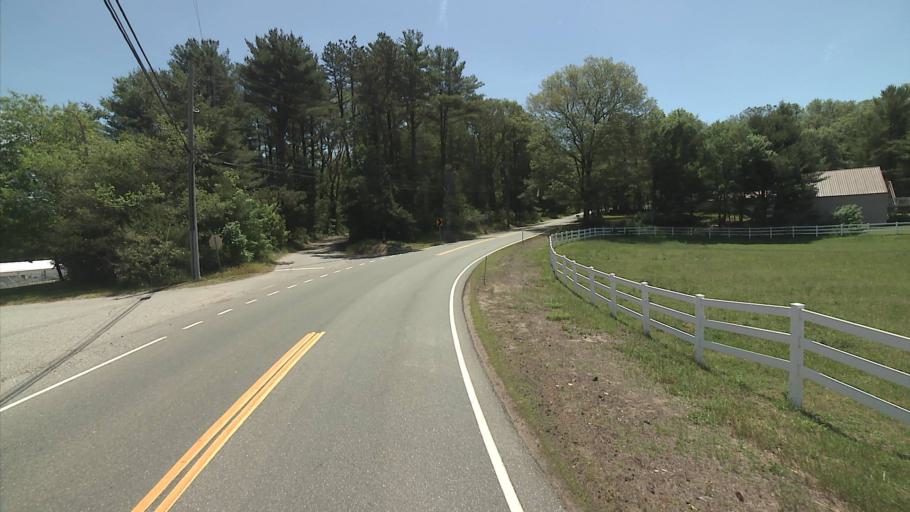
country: US
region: Rhode Island
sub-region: Washington County
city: Hopkinton
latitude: 41.5503
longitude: -71.8466
